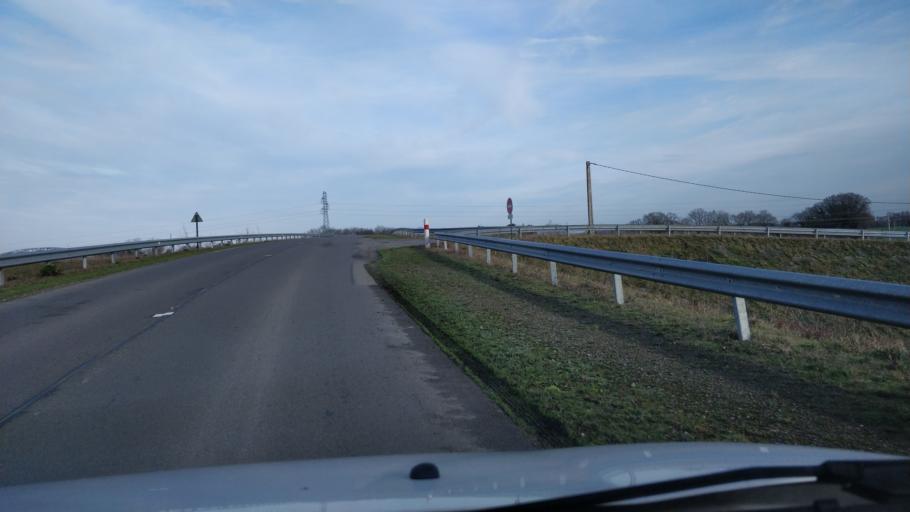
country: FR
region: Brittany
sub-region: Departement d'Ille-et-Vilaine
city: Argentre-du-Plessis
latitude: 48.0421
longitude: -1.1682
